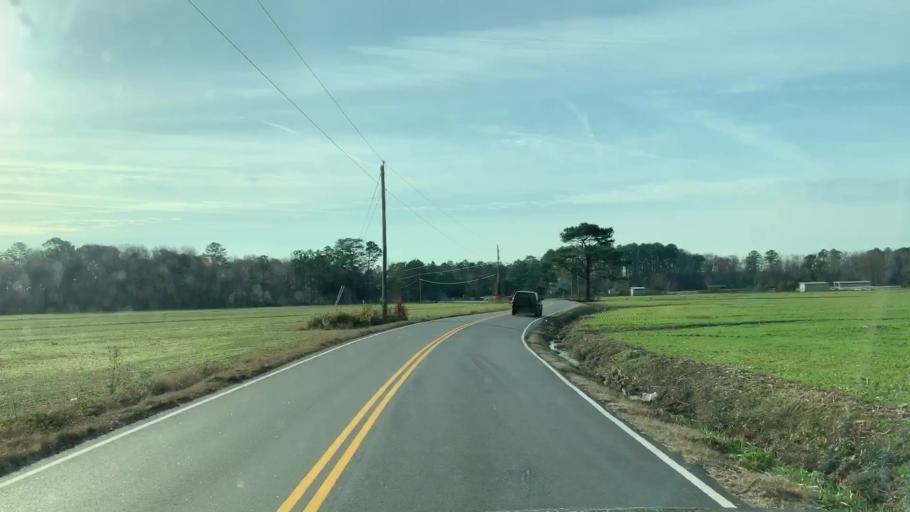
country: US
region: Virginia
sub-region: City of Virginia Beach
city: Virginia Beach
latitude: 36.7156
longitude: -76.0498
